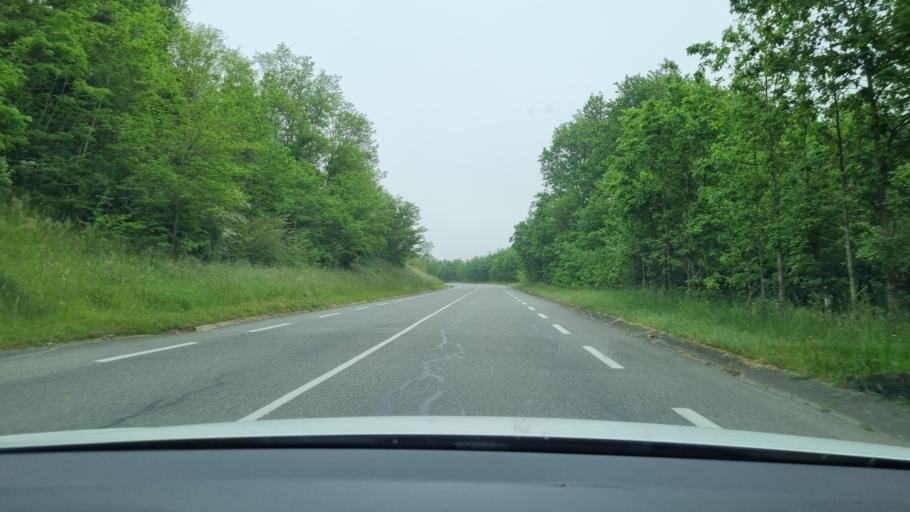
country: FR
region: Aquitaine
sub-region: Departement des Landes
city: Amou
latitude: 43.5501
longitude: -0.6791
